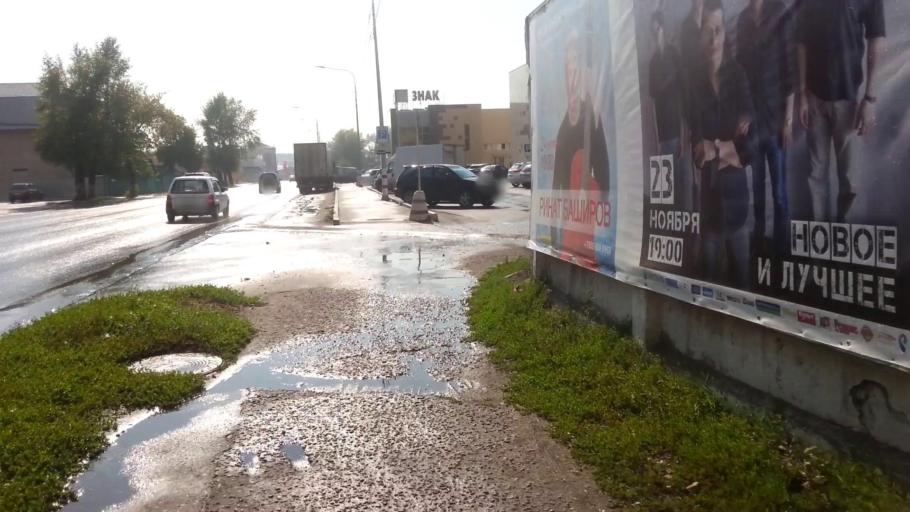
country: RU
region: Altai Krai
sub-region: Gorod Barnaulskiy
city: Barnaul
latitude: 53.3417
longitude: 83.7473
